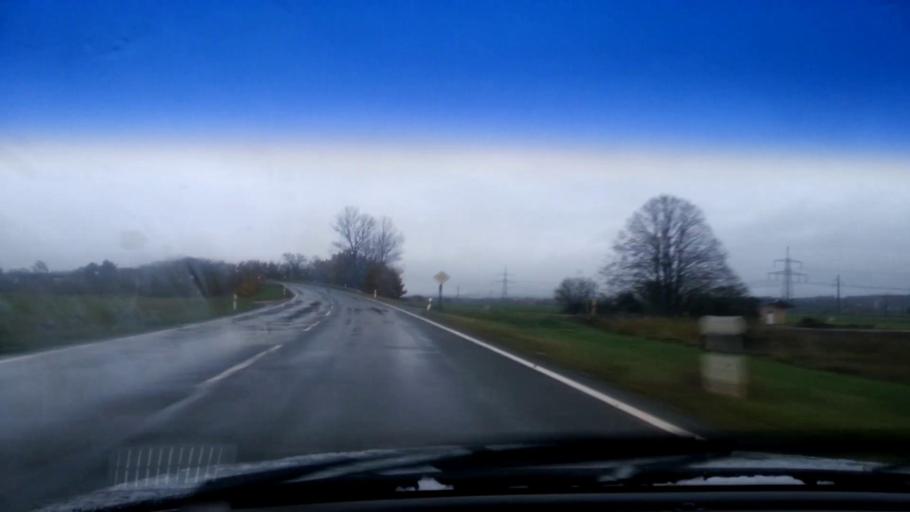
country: DE
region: Bavaria
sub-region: Upper Franconia
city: Oberhaid
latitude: 49.9344
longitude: 10.7965
